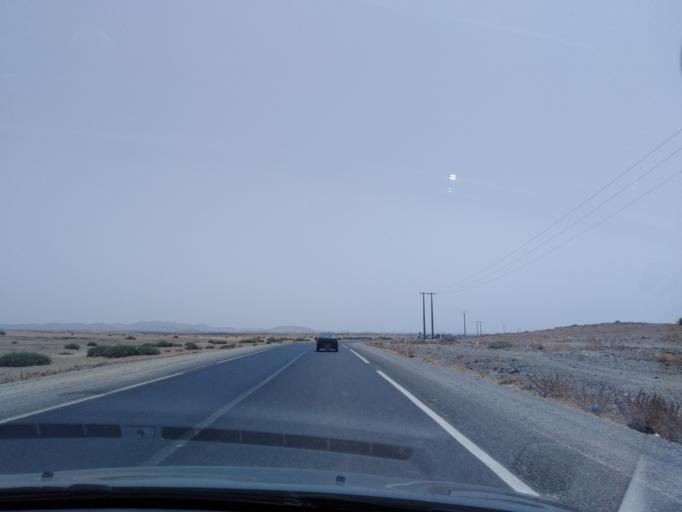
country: MA
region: Marrakech-Tensift-Al Haouz
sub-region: Kelaa-Des-Sraghna
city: Sidi Bou Othmane
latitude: 31.8169
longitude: -8.1570
